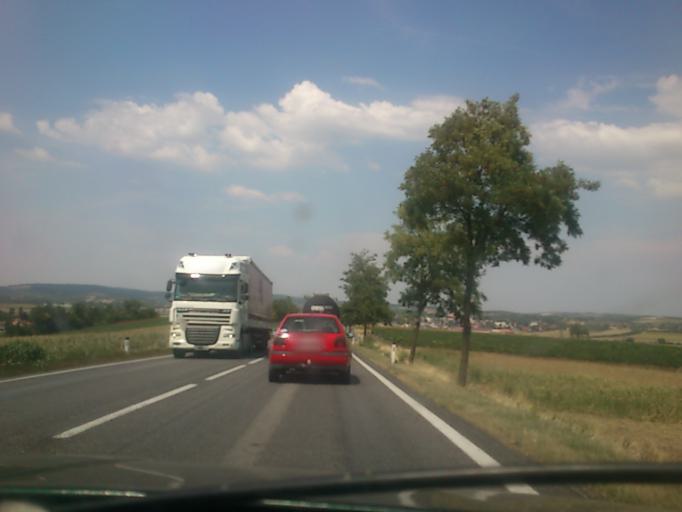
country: AT
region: Lower Austria
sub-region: Politischer Bezirk Mistelbach
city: Poysdorf
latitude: 48.6437
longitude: 16.6370
